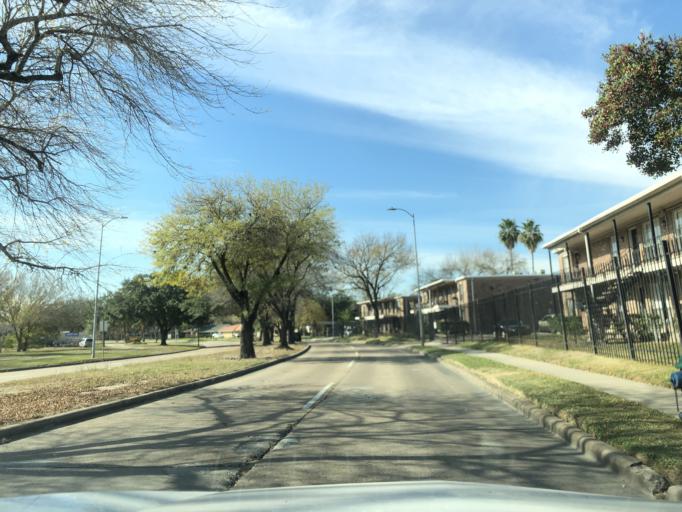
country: US
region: Texas
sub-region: Harris County
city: Bellaire
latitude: 29.6793
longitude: -95.4961
